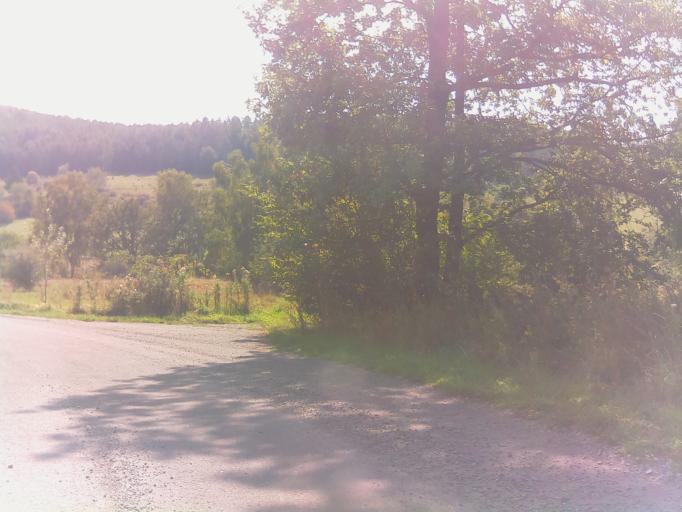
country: DE
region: Thuringia
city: Christes
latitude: 50.6442
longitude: 10.4650
